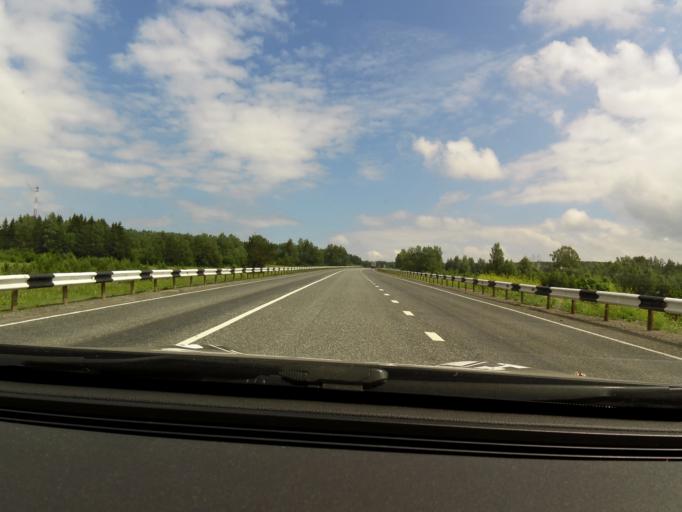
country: RU
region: Perm
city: Suksun
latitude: 57.0923
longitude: 57.3766
